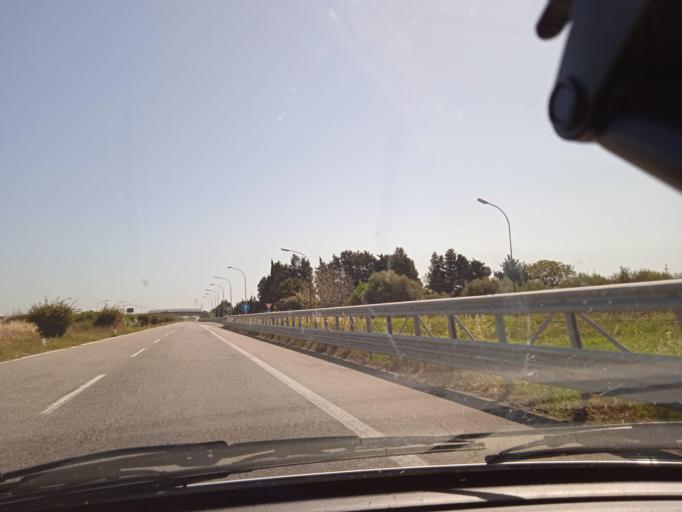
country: IT
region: Sicily
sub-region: Messina
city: Barcellona Pozzo di Gotto
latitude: 38.1562
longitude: 15.1884
